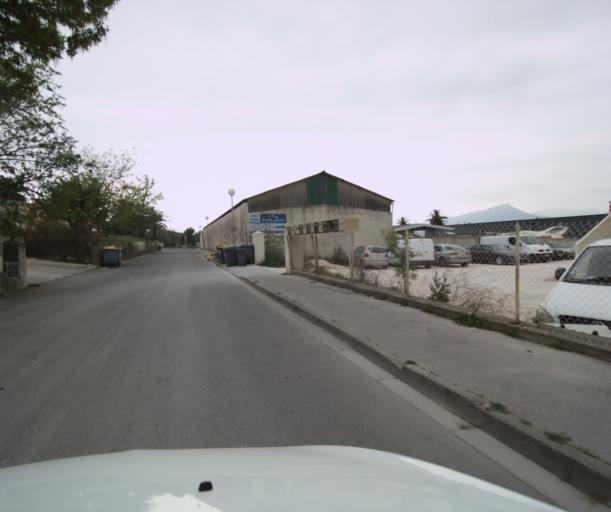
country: FR
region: Provence-Alpes-Cote d'Azur
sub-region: Departement du Var
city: Le Pradet
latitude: 43.1081
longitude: 6.0365
